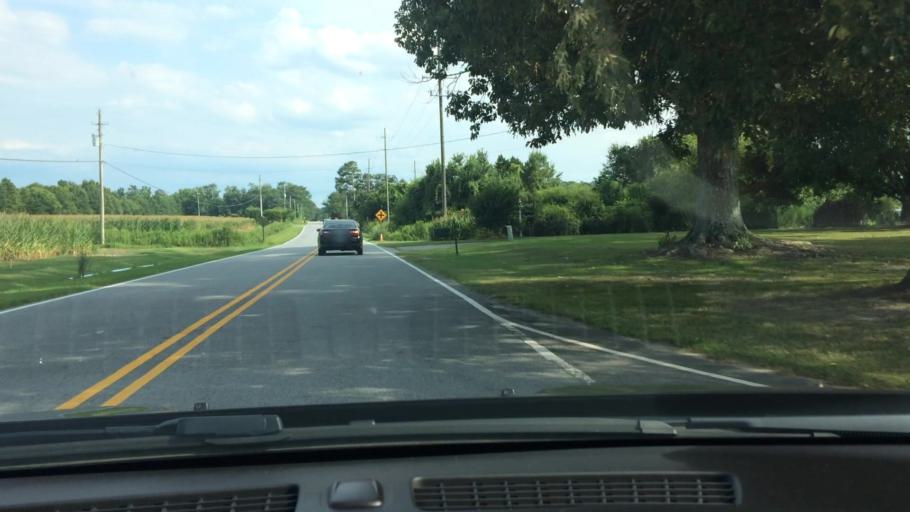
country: US
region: North Carolina
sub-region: Pitt County
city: Winterville
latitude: 35.5198
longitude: -77.3848
